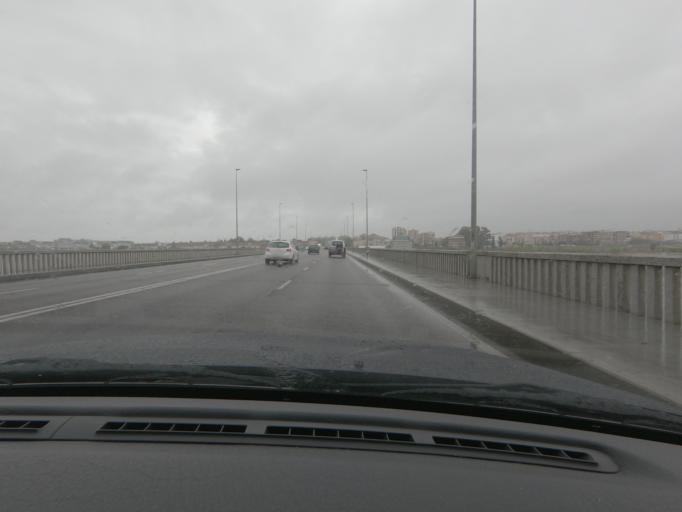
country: ES
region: Extremadura
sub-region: Provincia de Badajoz
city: Badajoz
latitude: 38.8794
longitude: -6.9814
